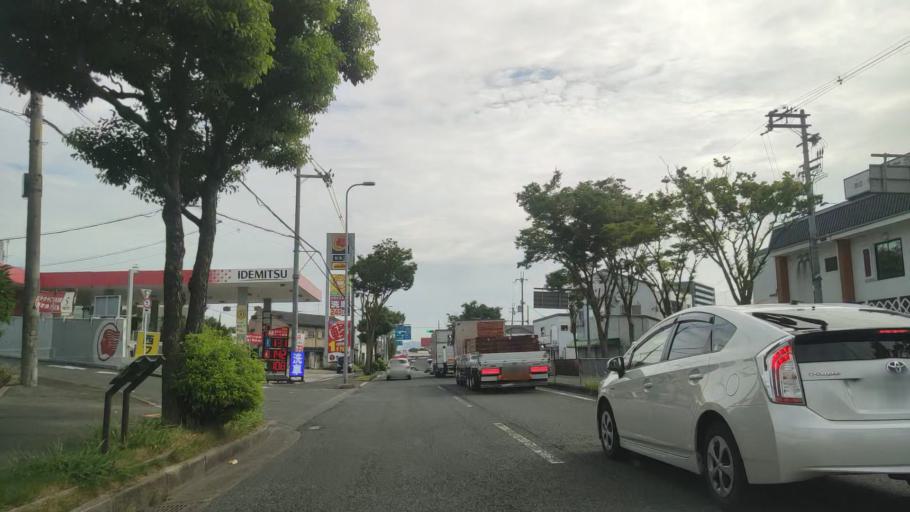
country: JP
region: Osaka
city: Tondabayashicho
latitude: 34.5044
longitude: 135.5951
